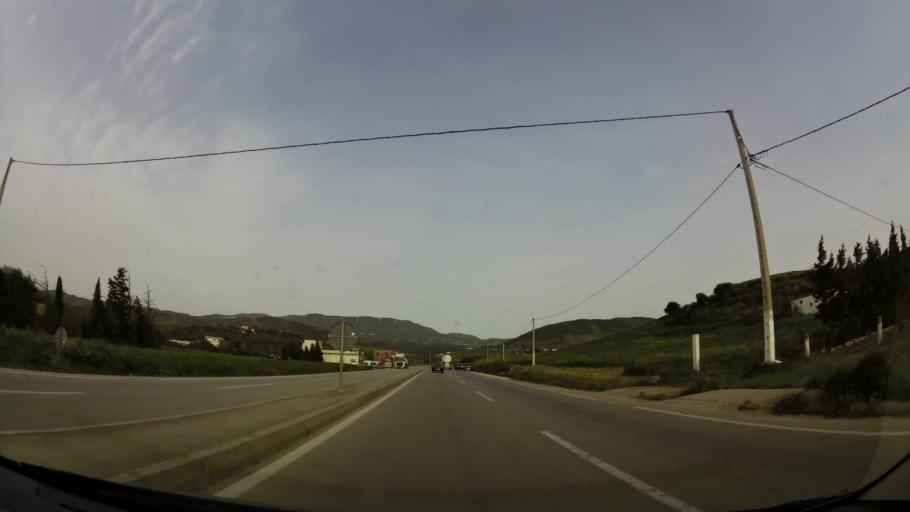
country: MA
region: Tanger-Tetouan
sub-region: Tanger-Assilah
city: Dar Chaoui
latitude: 35.5682
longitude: -5.6136
